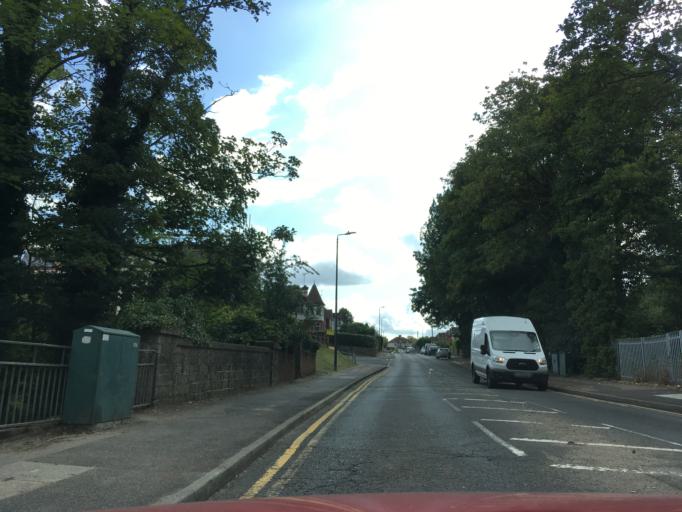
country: GB
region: England
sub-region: Kent
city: Maidstone
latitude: 51.2727
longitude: 0.5325
